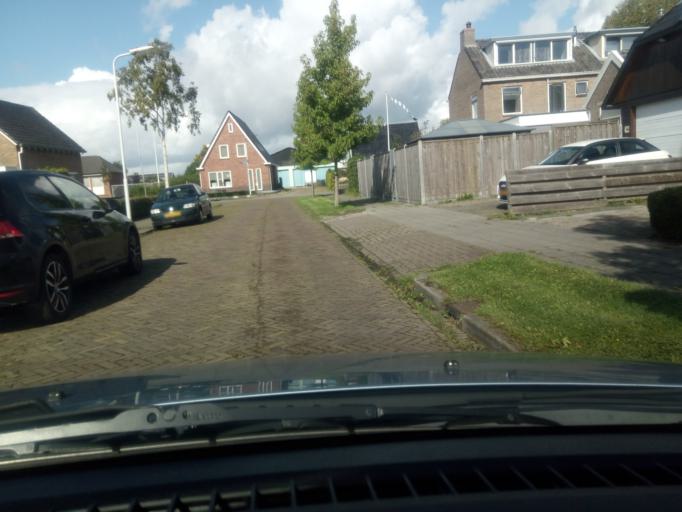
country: NL
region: Friesland
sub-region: Gemeente Achtkarspelen
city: Surhuisterveen
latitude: 53.1800
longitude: 6.1747
